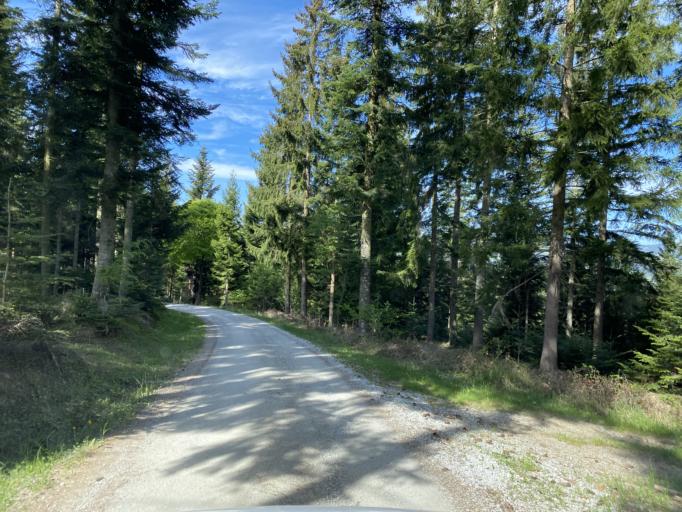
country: AT
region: Styria
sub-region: Politischer Bezirk Weiz
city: Gschaid bei Birkfeld
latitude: 47.3370
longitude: 15.7190
